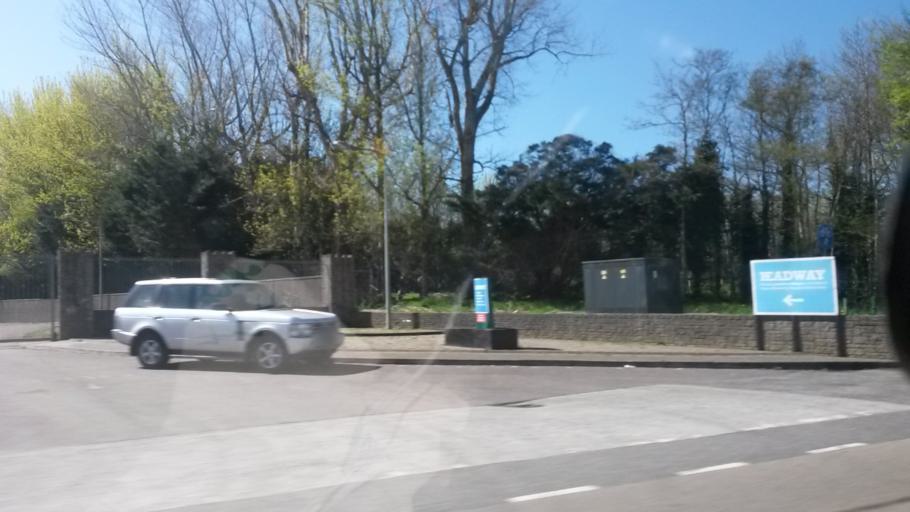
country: IE
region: Munster
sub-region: County Cork
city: Cork
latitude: 51.8938
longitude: -8.5165
